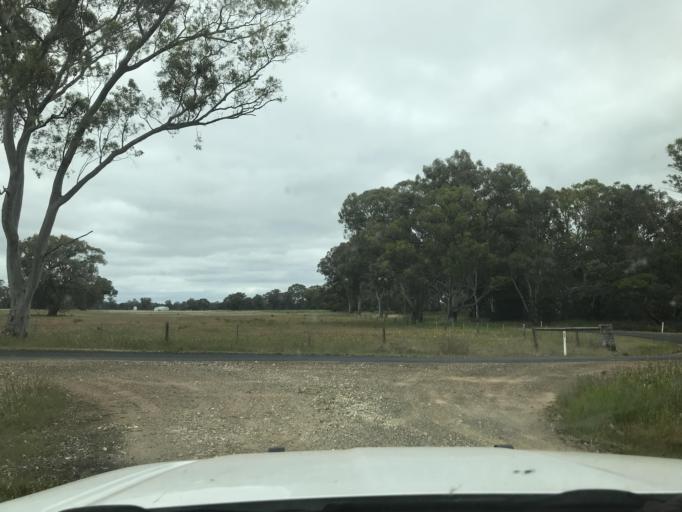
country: AU
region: South Australia
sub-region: Wattle Range
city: Penola
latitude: -37.1997
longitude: 140.9717
